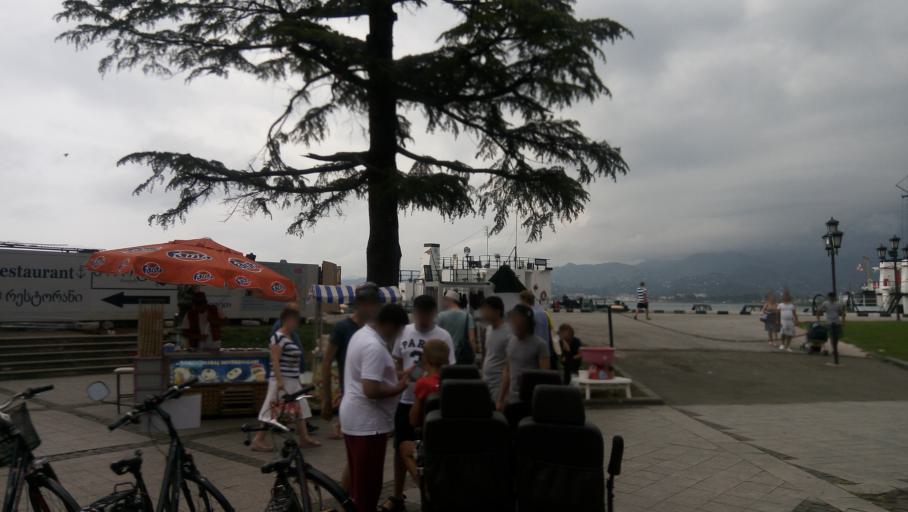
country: GE
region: Ajaria
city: Batumi
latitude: 41.6509
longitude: 41.6439
